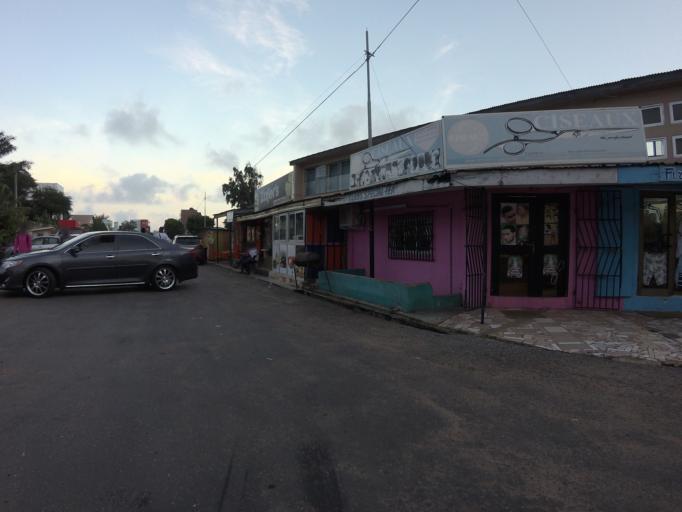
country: GH
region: Greater Accra
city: Accra
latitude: 5.5612
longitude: -0.1726
